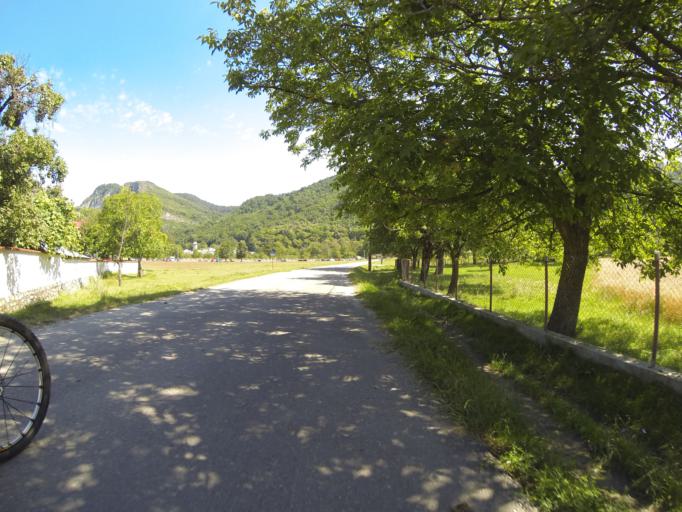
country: RO
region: Gorj
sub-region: Comuna Polovragi
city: Polovragi
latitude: 45.1895
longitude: 23.7892
